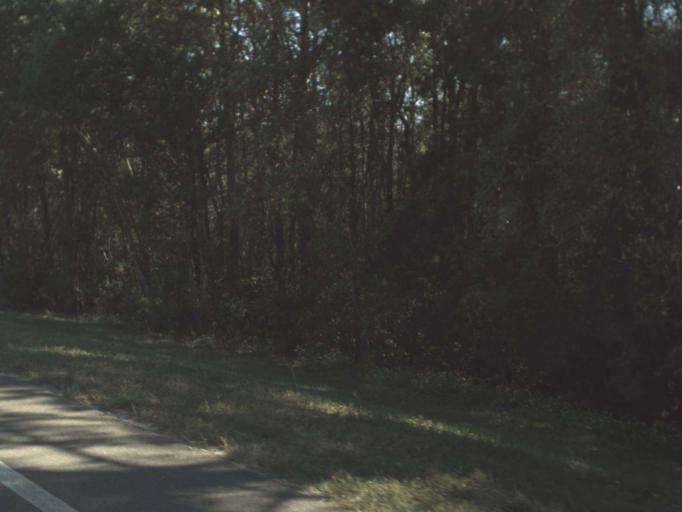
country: US
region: Florida
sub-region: Walton County
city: Freeport
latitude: 30.4938
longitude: -86.1270
